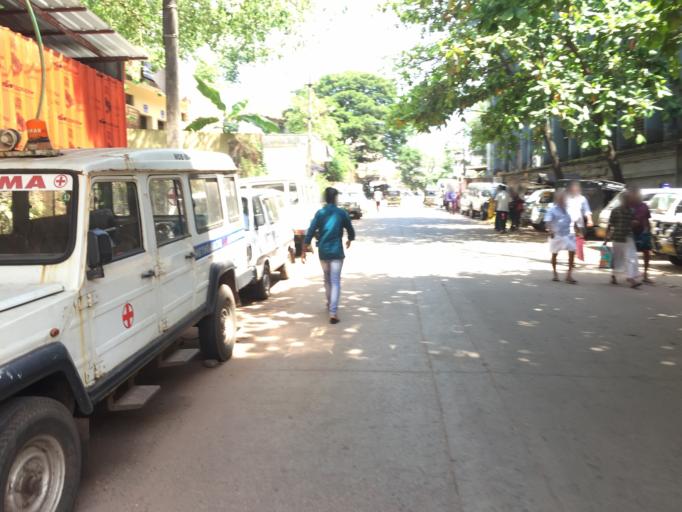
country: IN
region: Karnataka
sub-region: Dakshina Kannada
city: Mangalore
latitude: 12.8668
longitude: 74.8431
